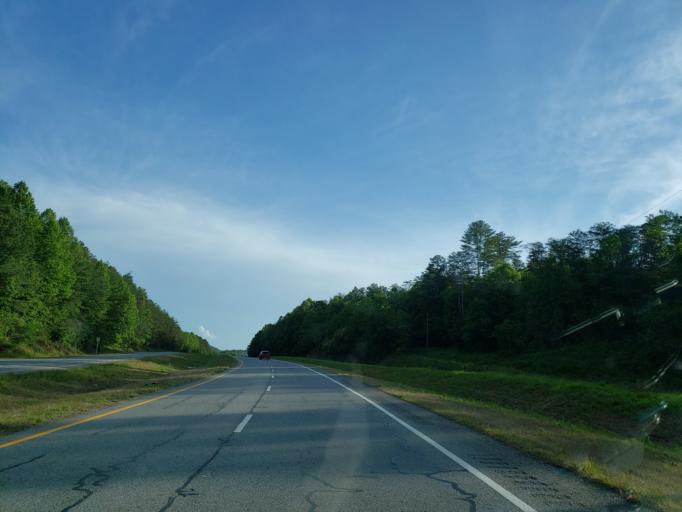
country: US
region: Georgia
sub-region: Fannin County
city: Blue Ridge
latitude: 34.7776
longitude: -84.3935
